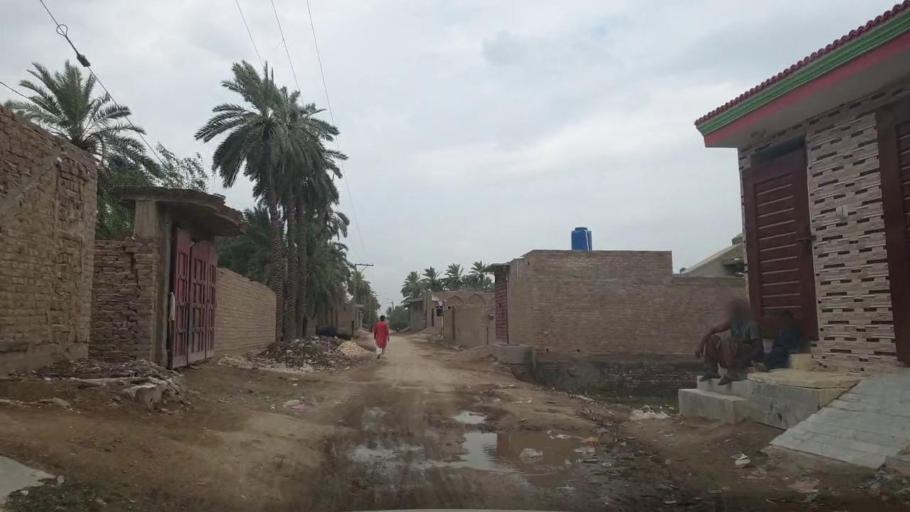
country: PK
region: Sindh
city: Khairpur
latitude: 27.5409
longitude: 68.7480
